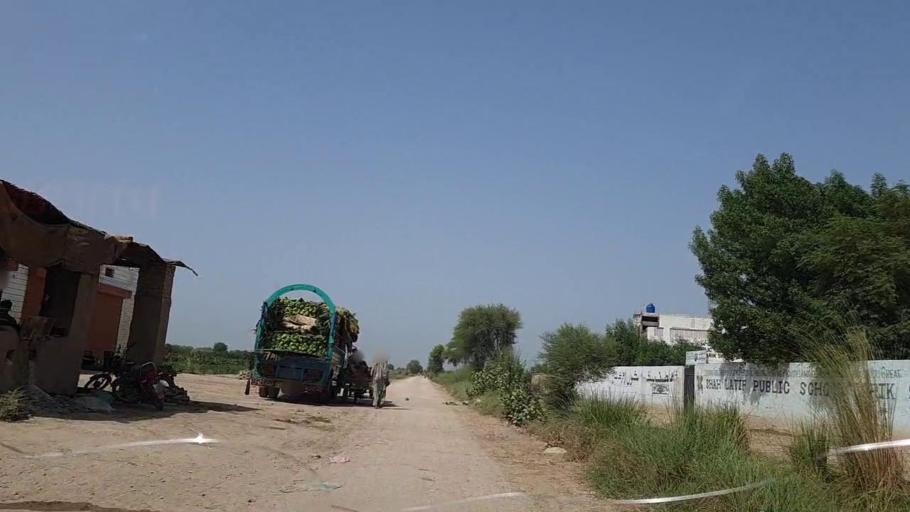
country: PK
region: Sindh
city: Kandiaro
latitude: 27.0306
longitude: 68.1538
